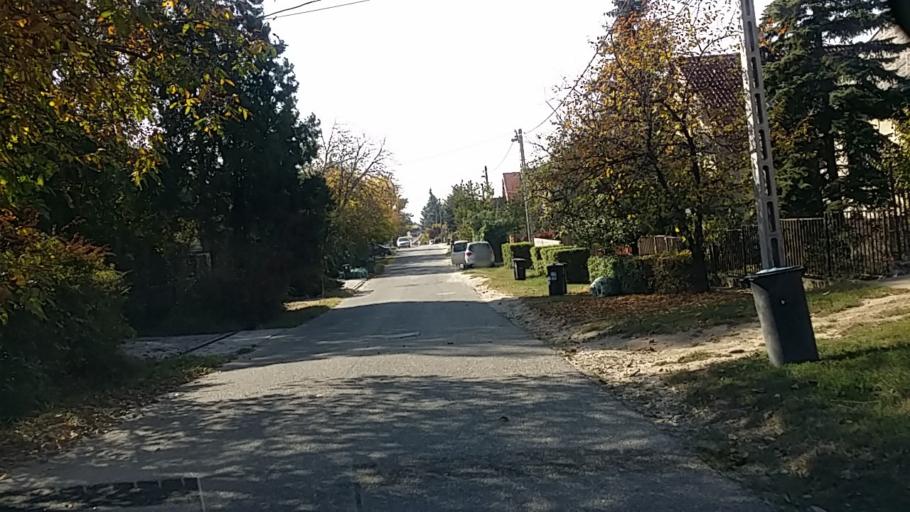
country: HU
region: Pest
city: Fot
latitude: 47.6087
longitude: 19.2076
